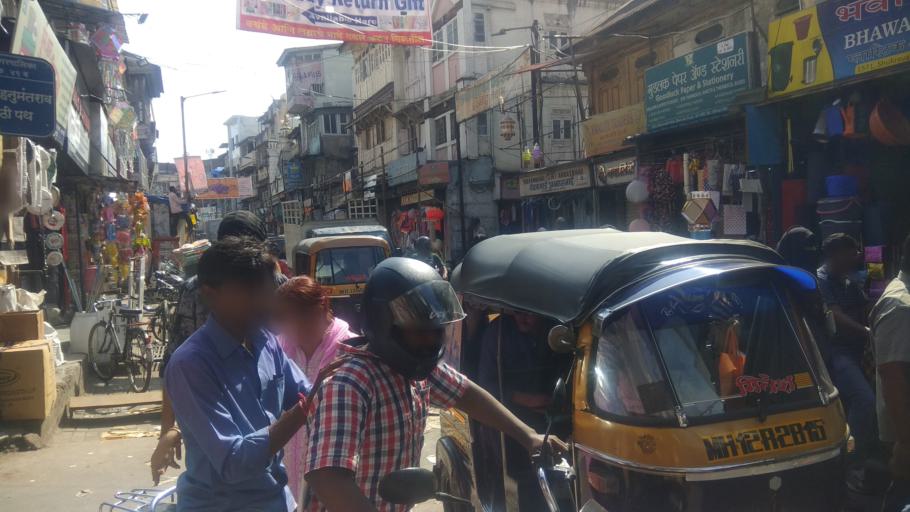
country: IN
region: Maharashtra
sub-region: Pune Division
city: Pune
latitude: 18.5138
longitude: 73.8595
